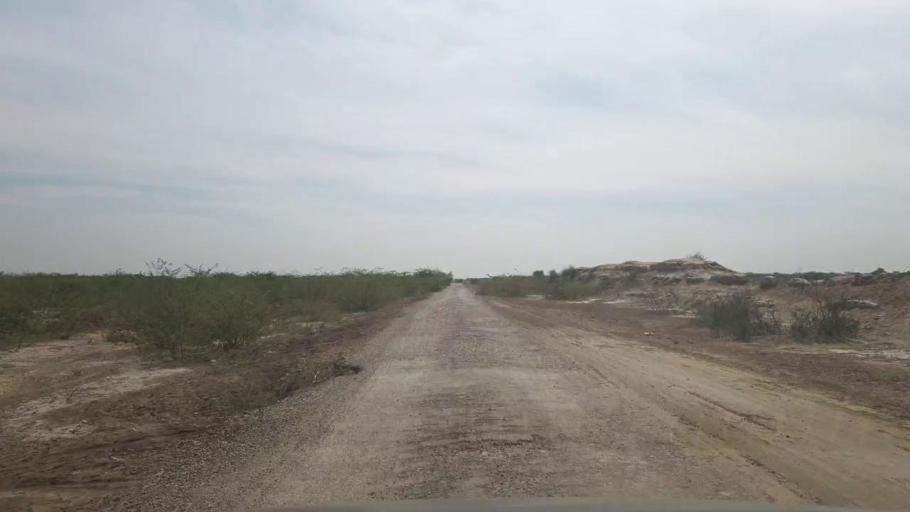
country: PK
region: Sindh
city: Kunri
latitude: 25.2621
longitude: 69.6038
